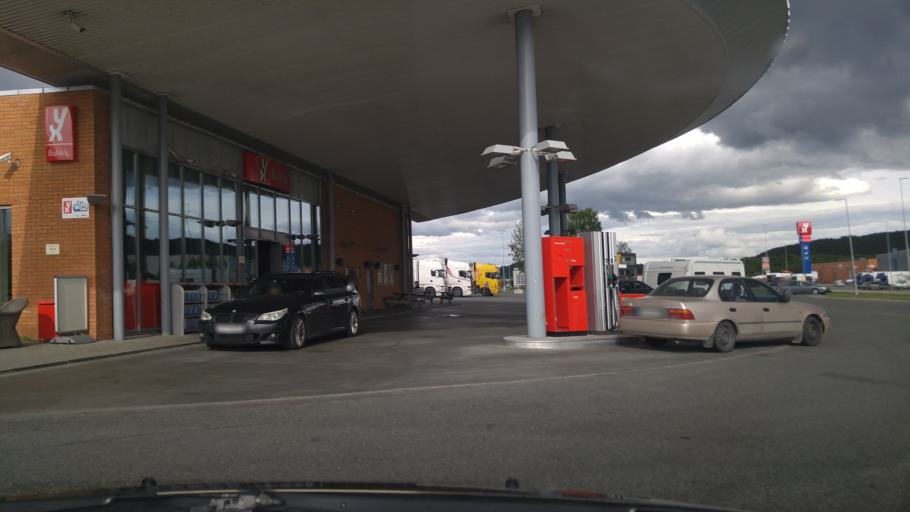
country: NO
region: Nord-Trondelag
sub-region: Levanger
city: Skogn
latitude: 63.7173
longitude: 11.2253
